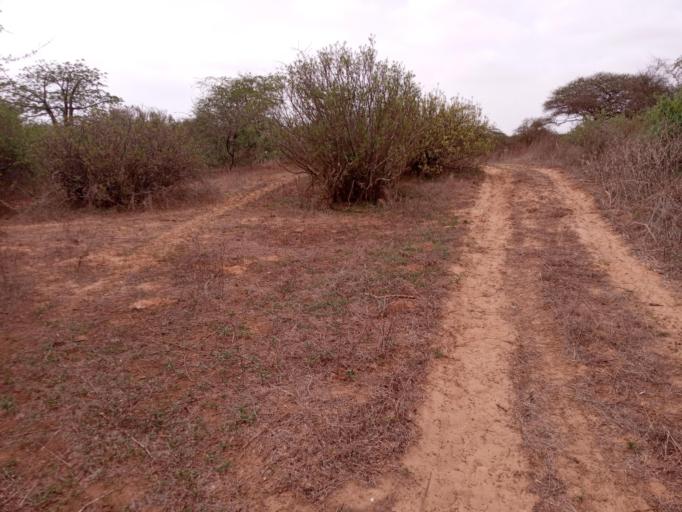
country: SN
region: Saint-Louis
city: Saint-Louis
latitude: 15.9233
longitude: -16.4533
